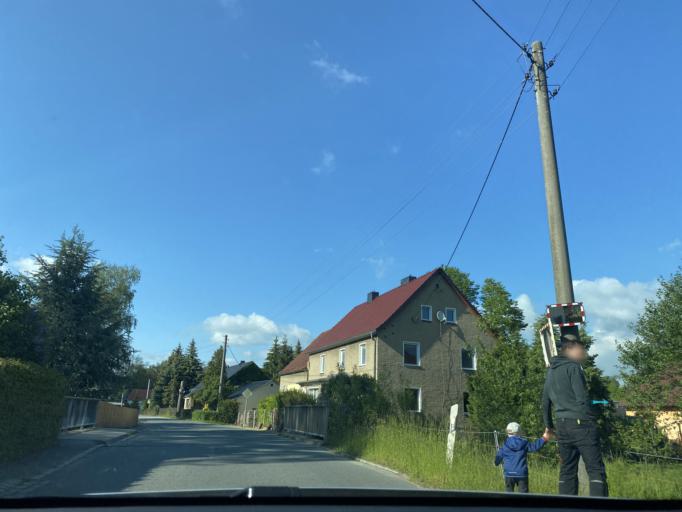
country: DE
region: Saxony
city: Markersdorf
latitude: 51.1350
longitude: 14.8800
